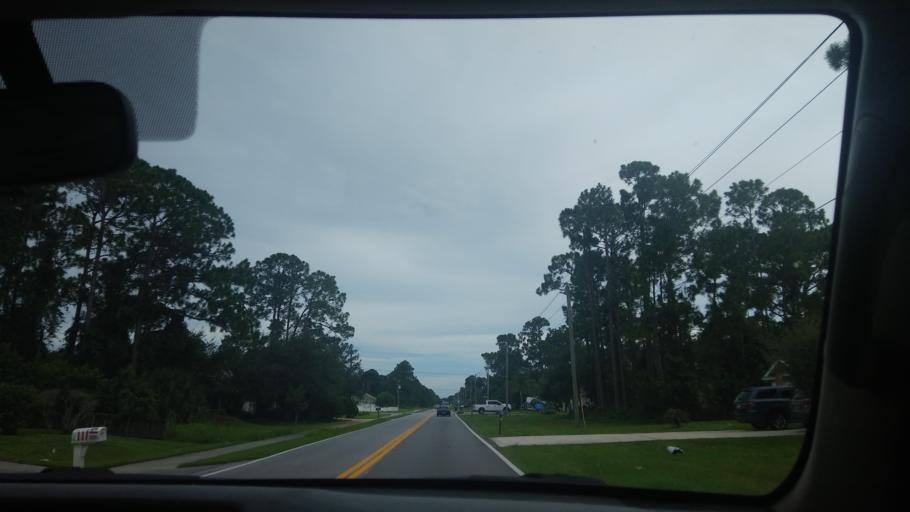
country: US
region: Florida
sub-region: Brevard County
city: Grant-Valkaria
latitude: 27.9738
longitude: -80.6347
